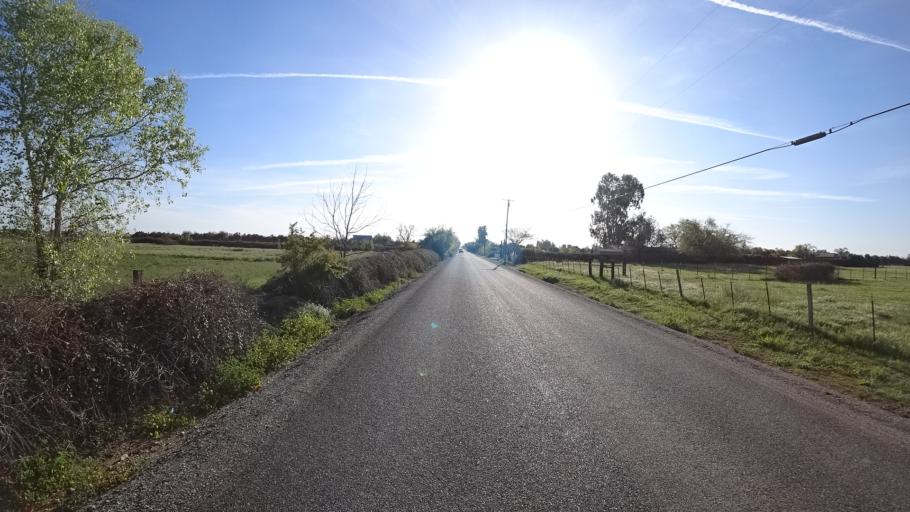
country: US
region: California
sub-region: Glenn County
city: Orland
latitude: 39.7260
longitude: -122.2247
